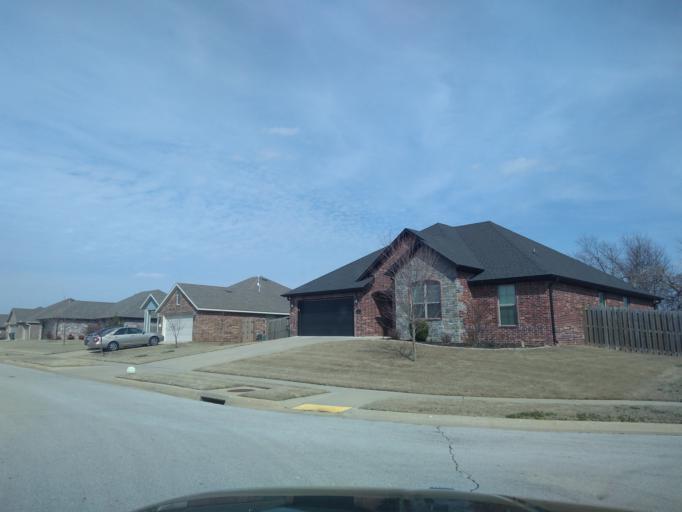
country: US
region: Arkansas
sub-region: Washington County
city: Farmington
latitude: 36.0688
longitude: -94.2462
